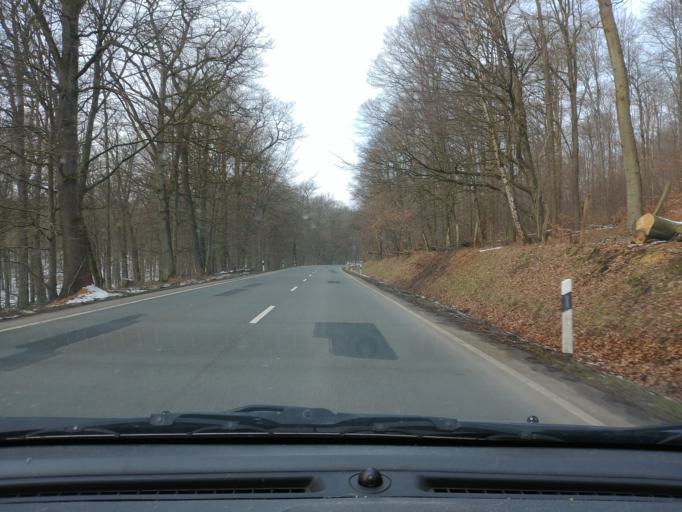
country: DE
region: Lower Saxony
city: Bad Karlshafen
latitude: 51.6873
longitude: 9.5029
